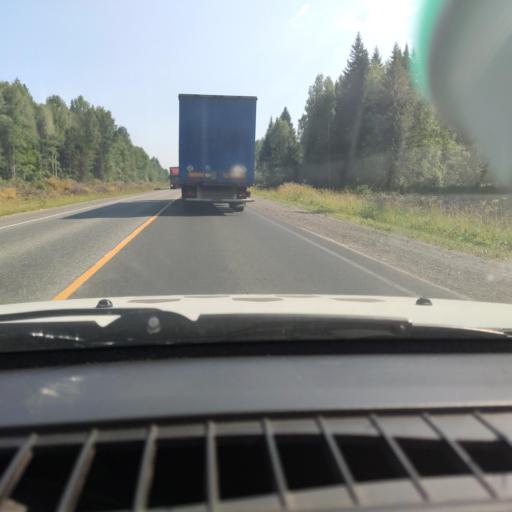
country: RU
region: Perm
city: Kukushtan
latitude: 57.5586
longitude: 56.5748
